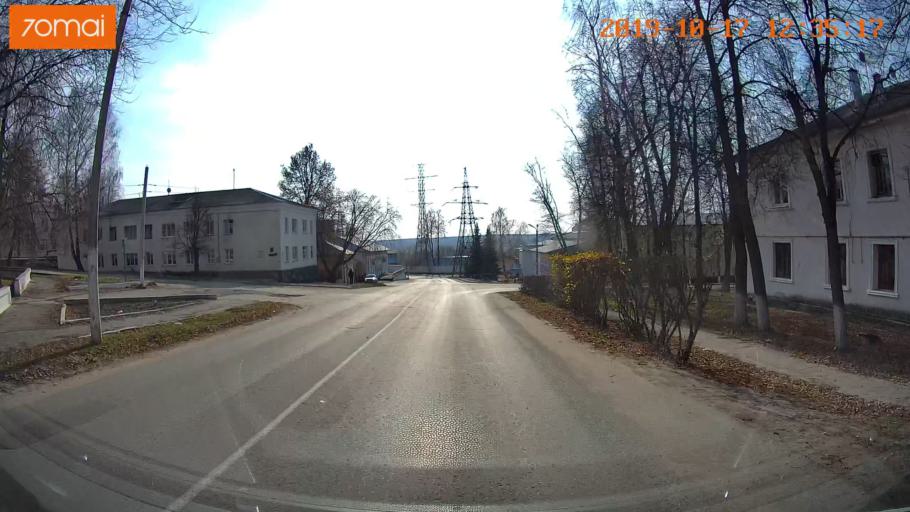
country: RU
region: Rjazan
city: Kasimov
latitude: 54.9445
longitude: 41.3700
